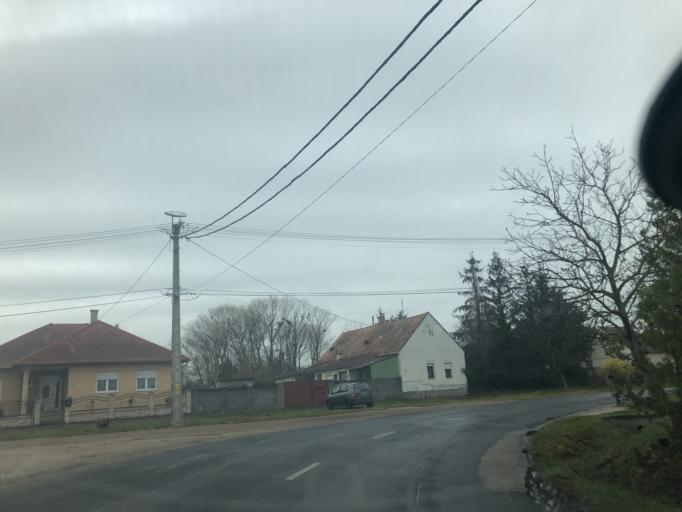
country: HU
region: Gyor-Moson-Sopron
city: Fertoszentmiklos
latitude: 47.6047
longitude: 16.9486
